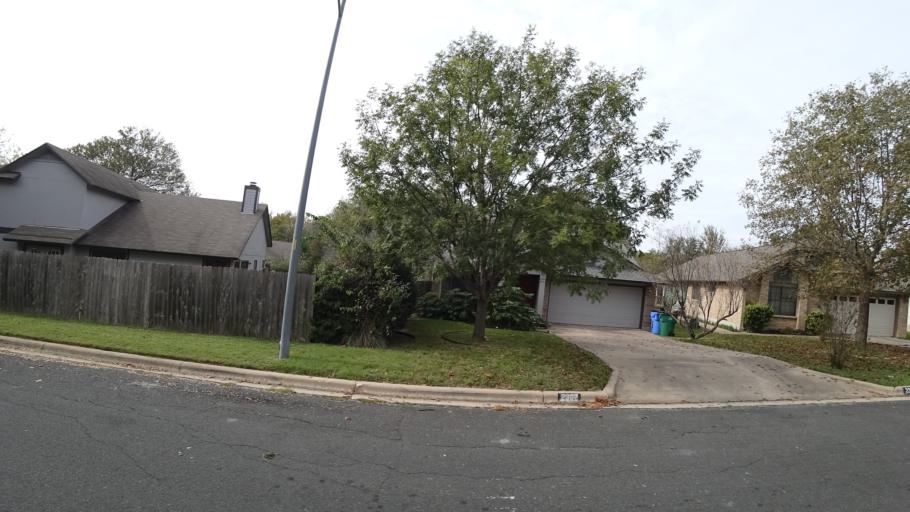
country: US
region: Texas
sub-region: Travis County
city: Wells Branch
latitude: 30.4488
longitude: -97.6793
